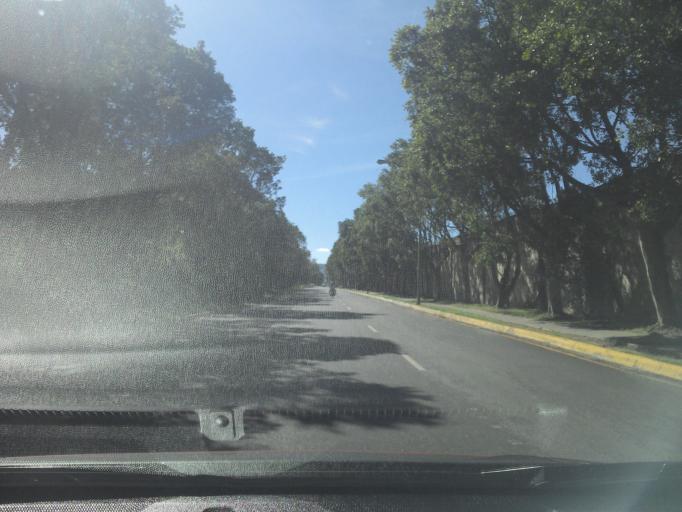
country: MX
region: Jalisco
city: Zapopan2
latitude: 20.7138
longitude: -103.4333
